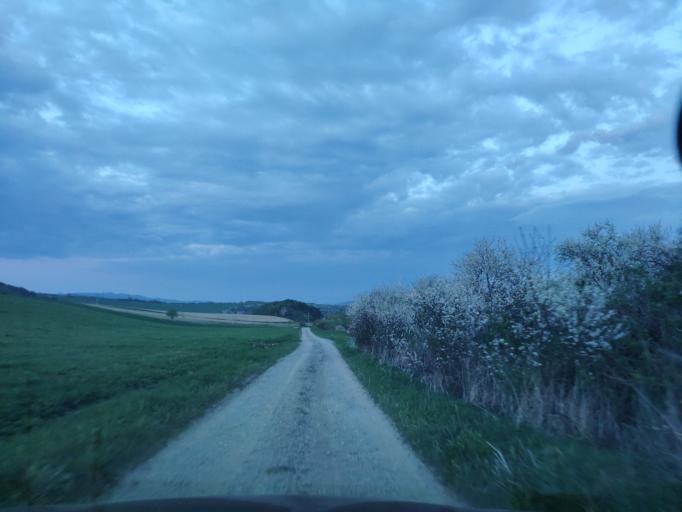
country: SK
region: Presovsky
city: Lipany
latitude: 49.1806
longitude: 20.8450
